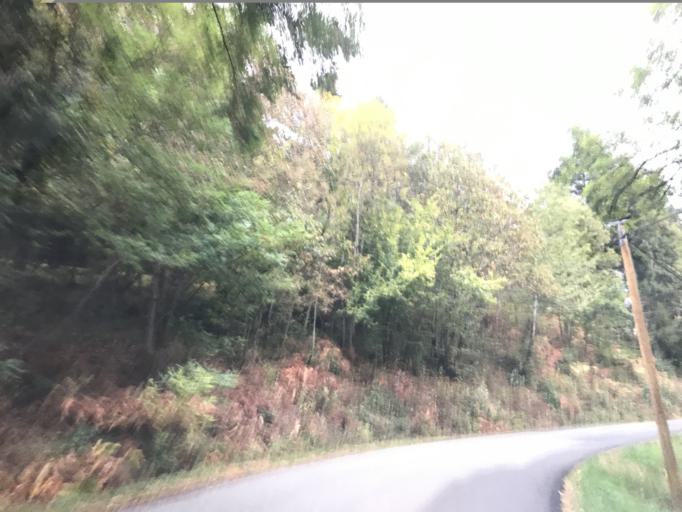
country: FR
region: Auvergne
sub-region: Departement du Puy-de-Dome
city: Thiers
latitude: 45.8354
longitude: 3.5753
